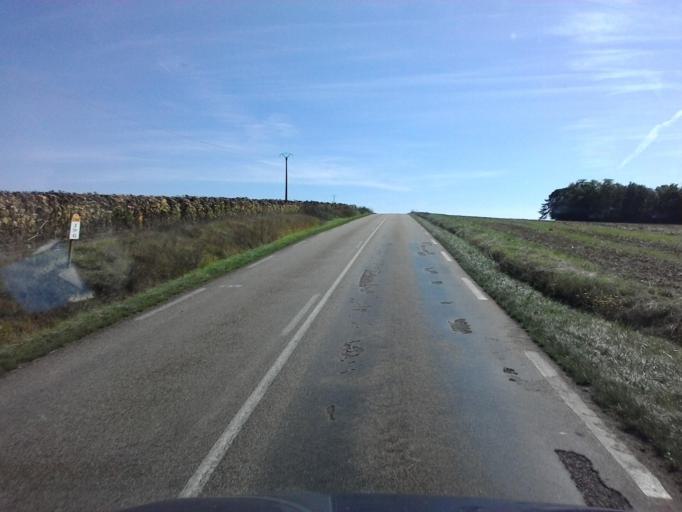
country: FR
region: Bourgogne
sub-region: Departement de l'Yonne
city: Joux-la-Ville
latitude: 47.5761
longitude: 3.8787
